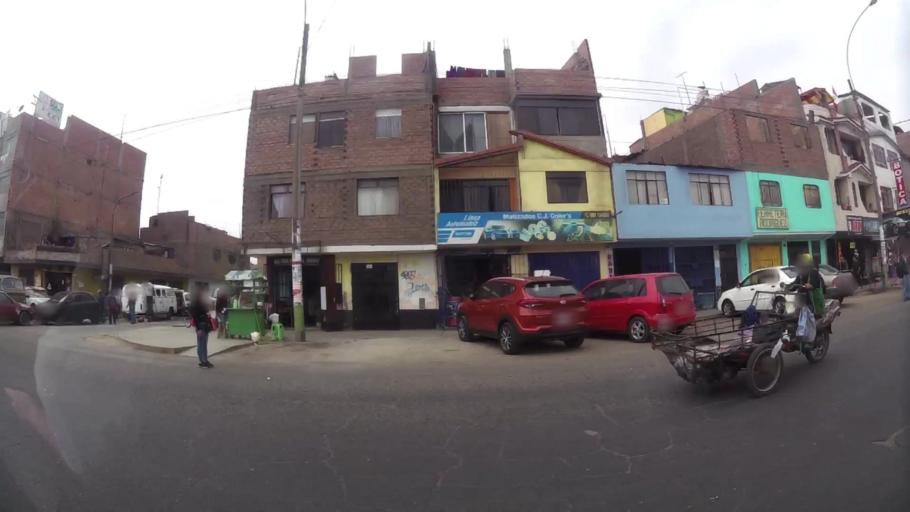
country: PE
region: Callao
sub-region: Callao
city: Callao
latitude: -12.0285
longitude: -77.0964
